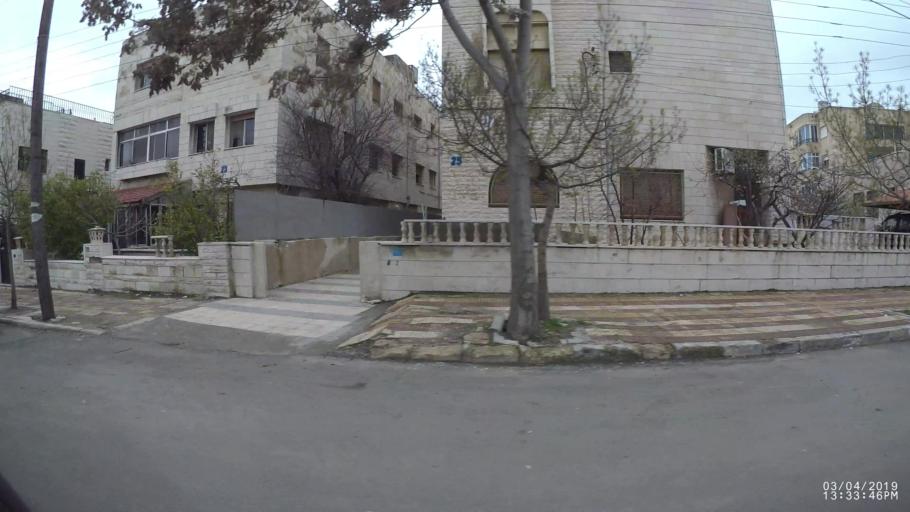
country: JO
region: Amman
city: Wadi as Sir
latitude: 31.9698
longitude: 35.8374
